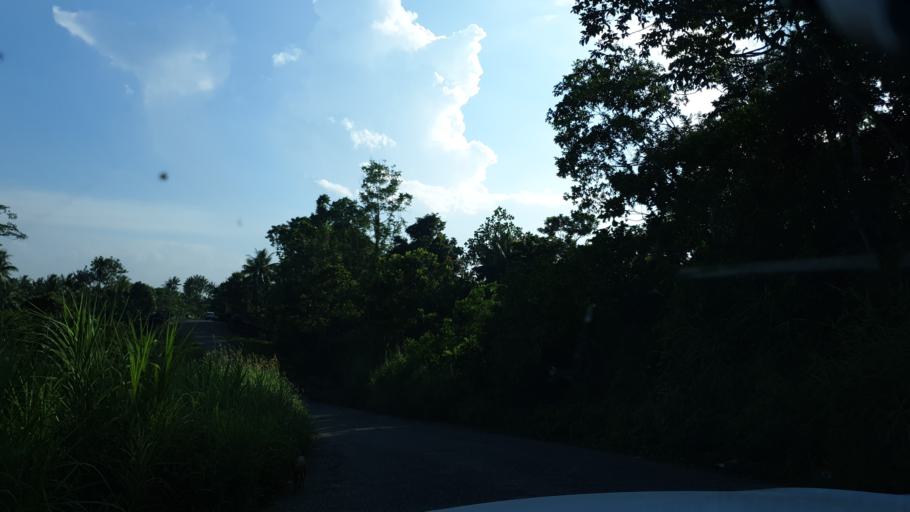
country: PG
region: East Sepik
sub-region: Wewak
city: Wewak
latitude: -3.7004
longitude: 143.6440
